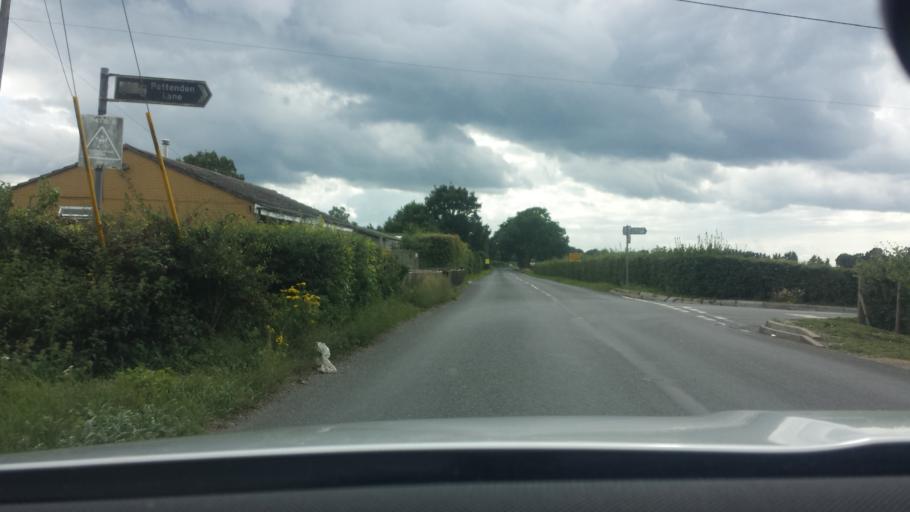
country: GB
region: England
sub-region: Kent
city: Marden
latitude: 51.1921
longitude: 0.5141
